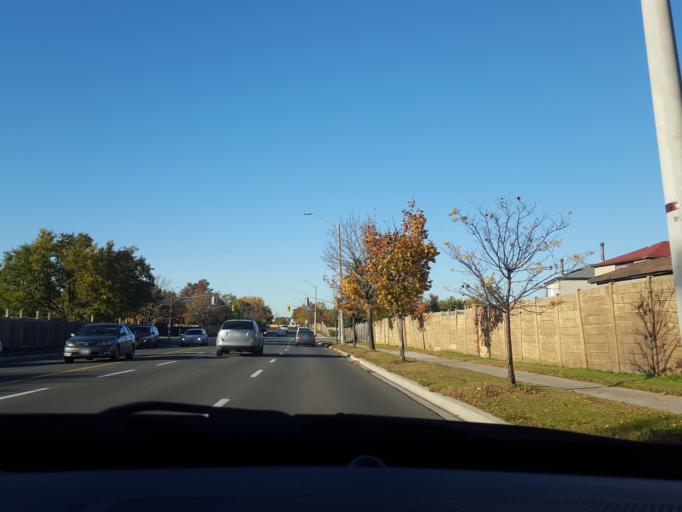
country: CA
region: Ontario
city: Markham
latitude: 43.8357
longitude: -79.2894
